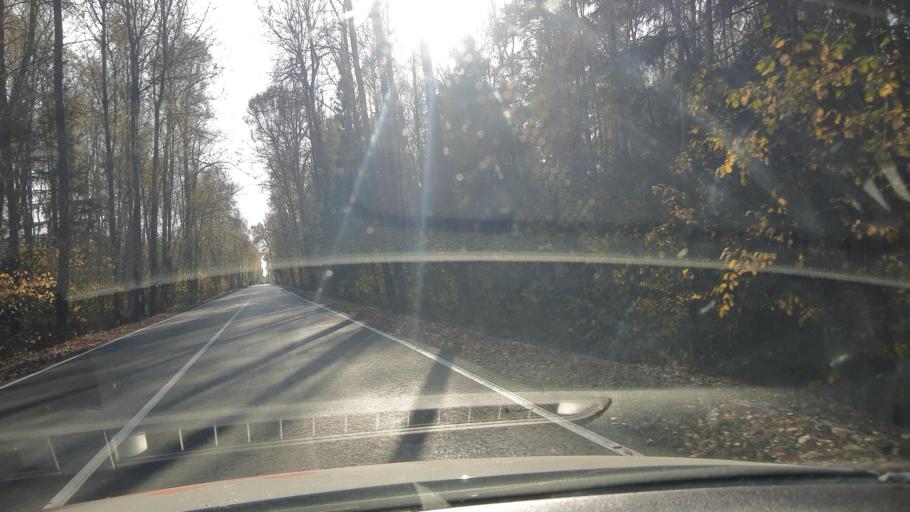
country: RU
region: Moskovskaya
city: Imeni Vorovskogo
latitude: 55.7909
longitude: 38.3664
